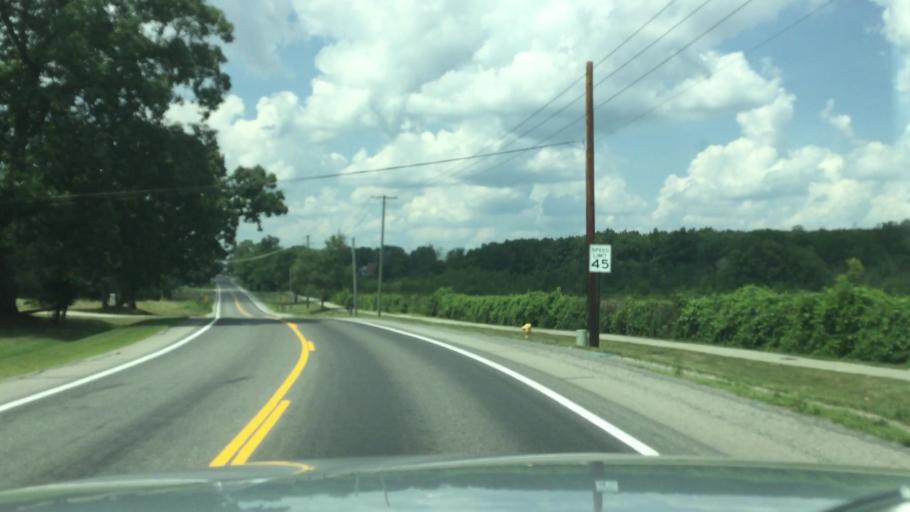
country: US
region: Michigan
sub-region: Washtenaw County
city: Ypsilanti
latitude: 42.2041
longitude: -83.6105
